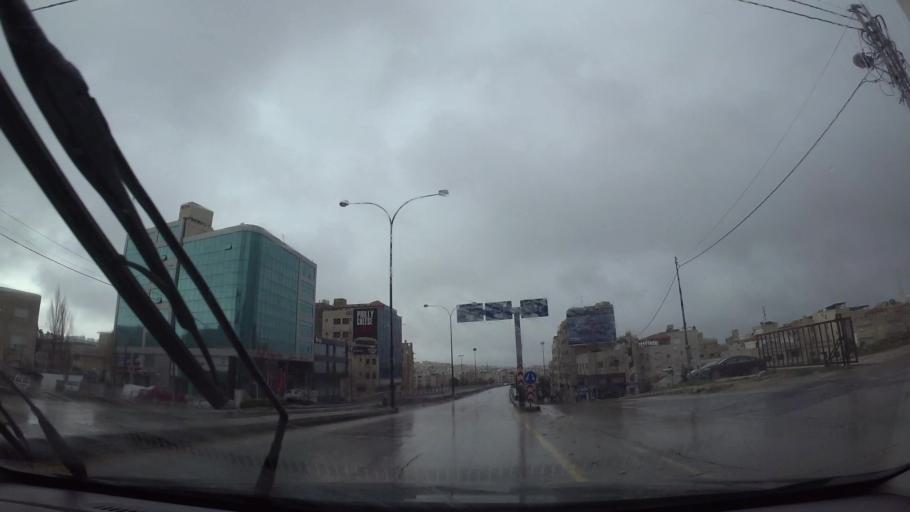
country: JO
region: Amman
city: Al Jubayhah
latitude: 31.9764
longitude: 35.8656
